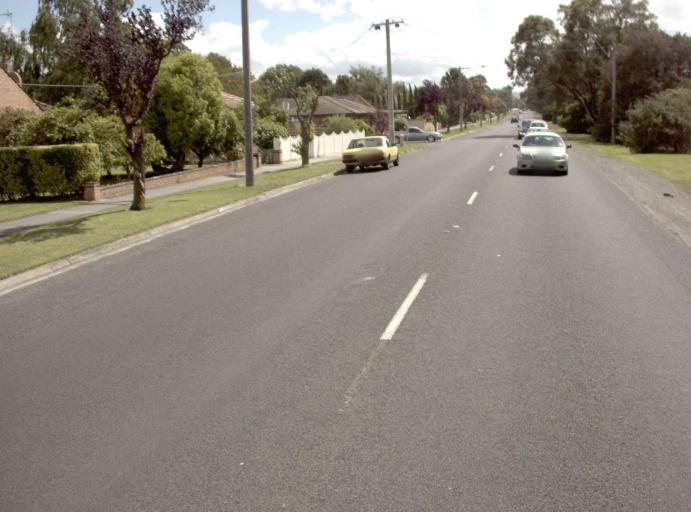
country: AU
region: Victoria
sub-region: Latrobe
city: Moe
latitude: -38.1809
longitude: 146.2477
